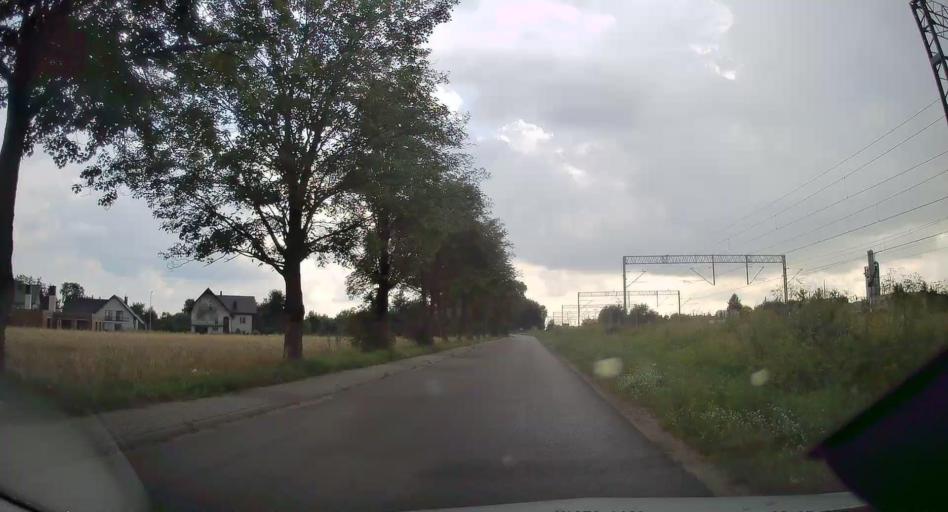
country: PL
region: Lodz Voivodeship
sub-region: Powiat brzezinski
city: Rogow
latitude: 51.8203
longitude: 19.8897
